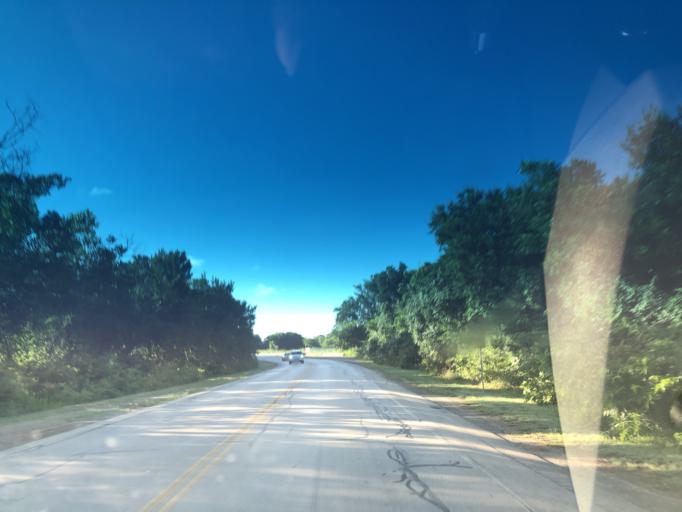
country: US
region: Texas
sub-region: Dallas County
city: Grand Prairie
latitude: 32.7788
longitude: -97.0153
